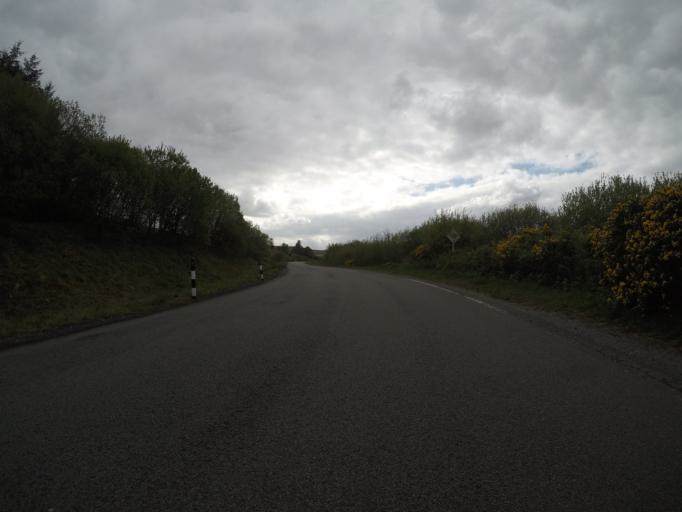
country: GB
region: Scotland
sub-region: Highland
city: Isle of Skye
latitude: 57.2988
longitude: -6.3048
